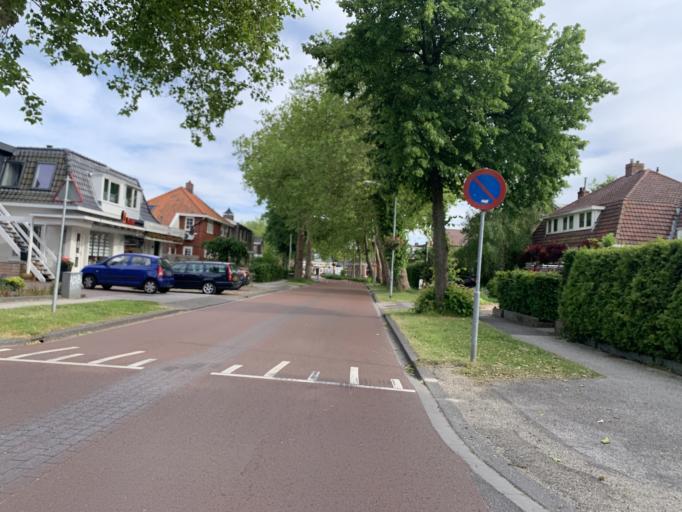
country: NL
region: Groningen
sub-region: Gemeente Haren
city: Haren
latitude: 53.1747
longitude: 6.6084
